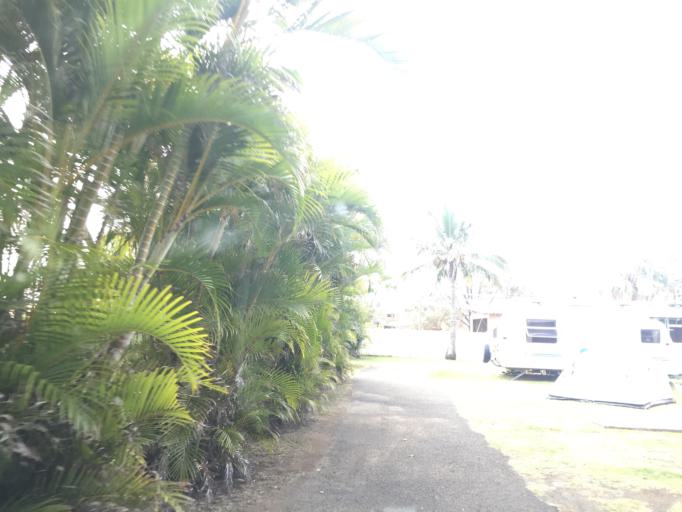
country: AU
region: Queensland
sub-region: Bundaberg
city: Bundaberg
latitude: -24.8339
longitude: 152.4717
